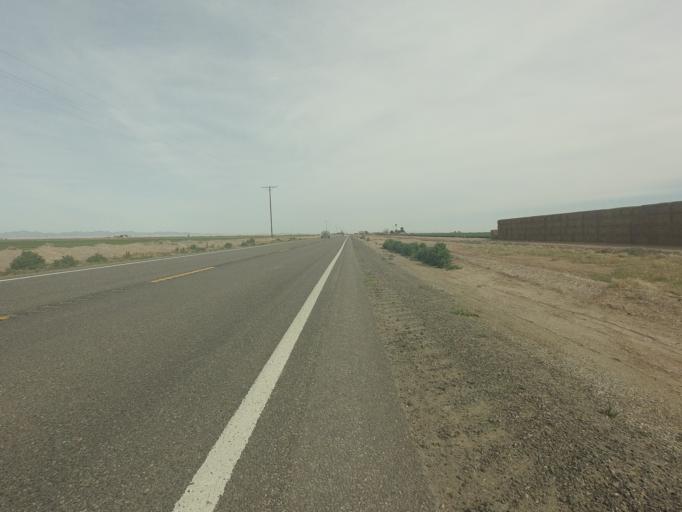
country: US
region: California
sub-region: Imperial County
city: Brawley
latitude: 32.9745
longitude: -115.3873
